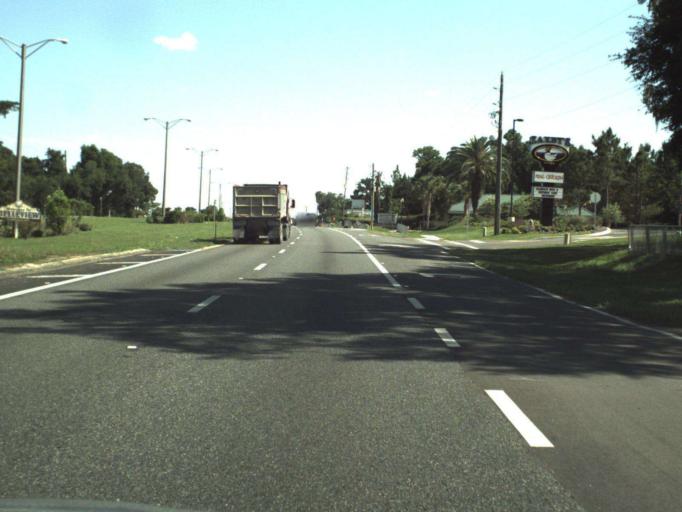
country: US
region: Florida
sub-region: Marion County
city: Belleview
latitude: 29.0700
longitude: -82.0710
